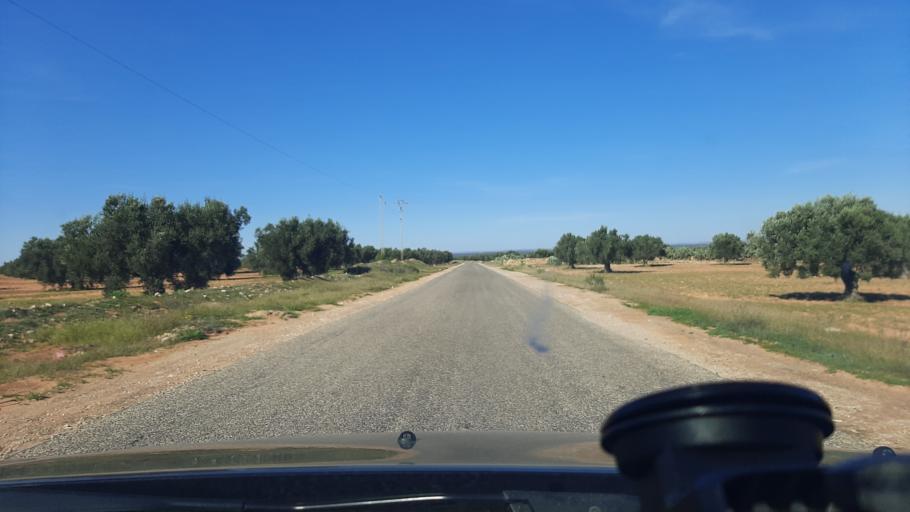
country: TN
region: Safaqis
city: Sfax
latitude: 34.9628
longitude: 10.5403
